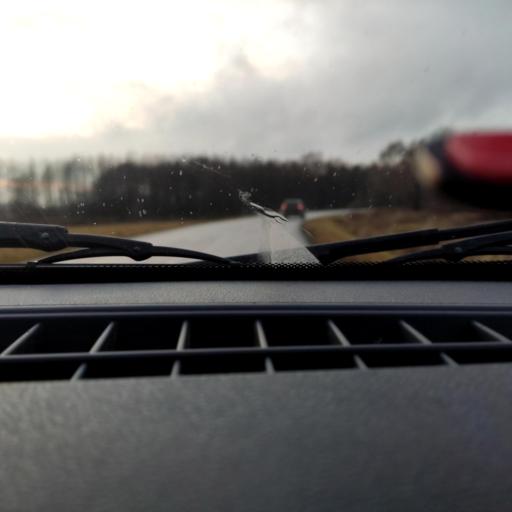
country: RU
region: Bashkortostan
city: Avdon
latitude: 54.5096
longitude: 55.8704
